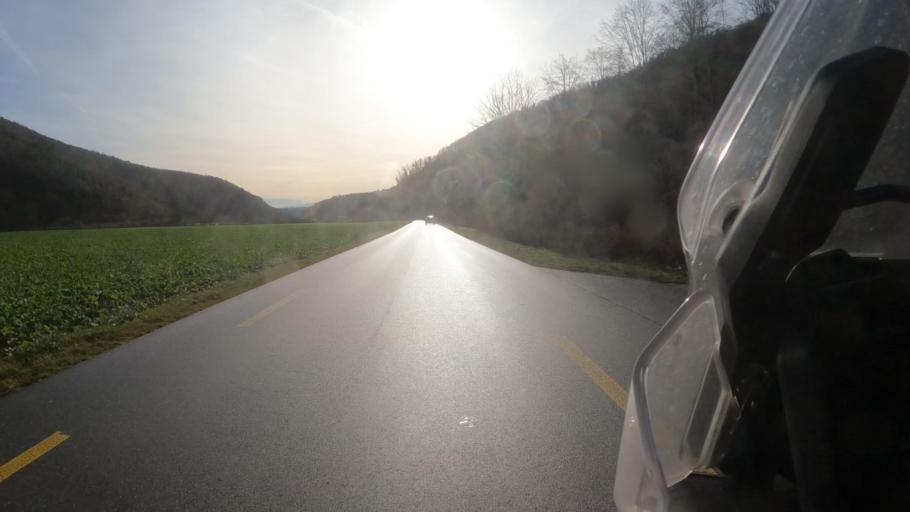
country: CH
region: Schaffhausen
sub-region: Bezirk Reiat
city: Stetten
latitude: 47.7428
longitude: 8.6181
